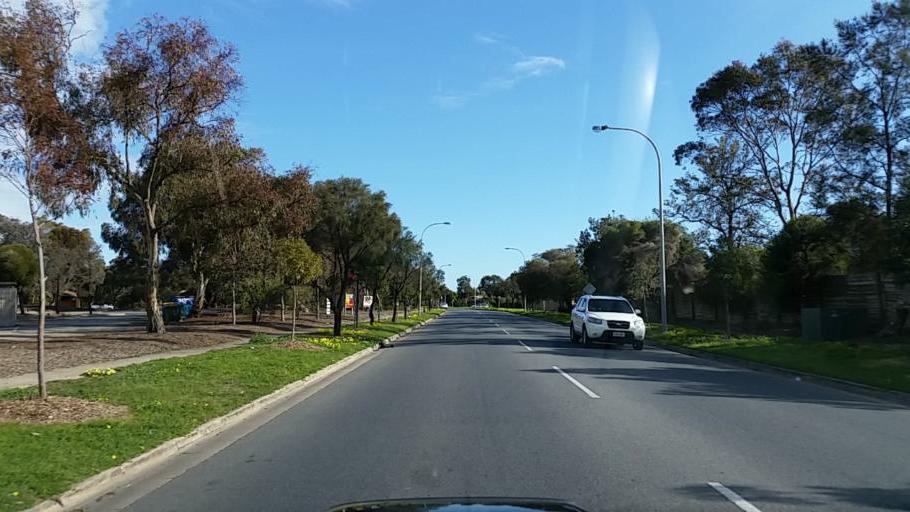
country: AU
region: South Australia
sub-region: Charles Sturt
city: West Lakes Shore
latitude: -34.8652
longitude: 138.4852
